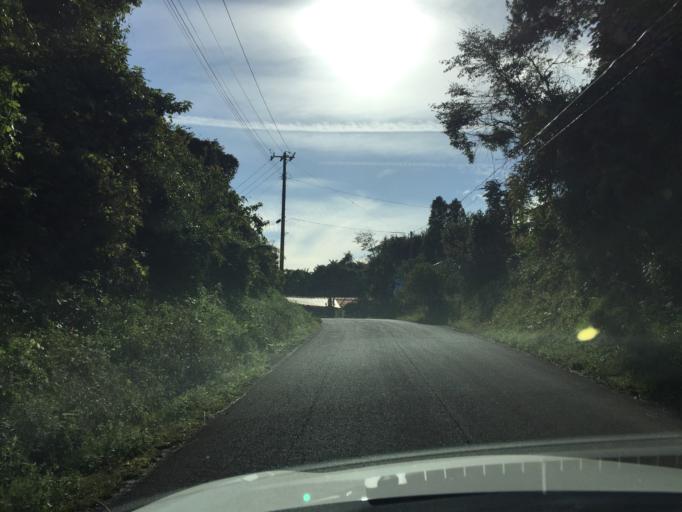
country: JP
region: Fukushima
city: Miharu
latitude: 37.3432
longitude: 140.4956
